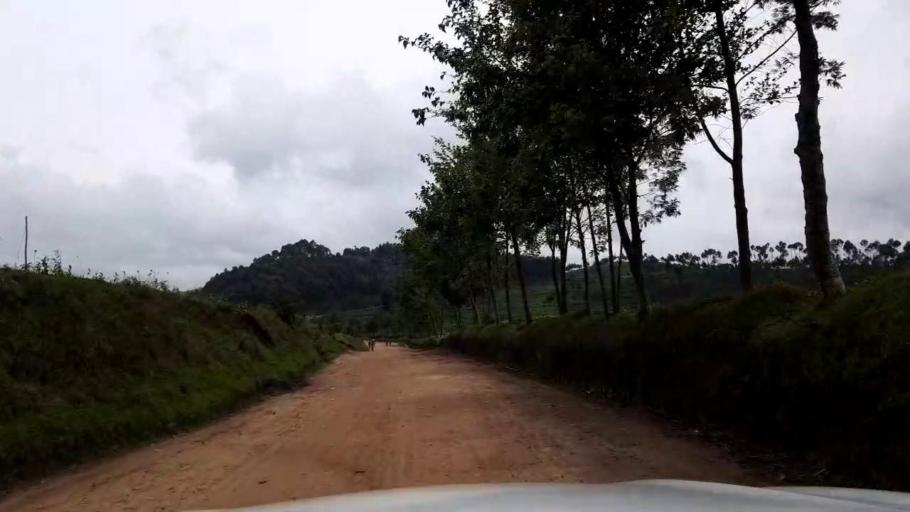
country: RW
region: Western Province
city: Kibuye
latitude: -1.9539
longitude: 29.4061
